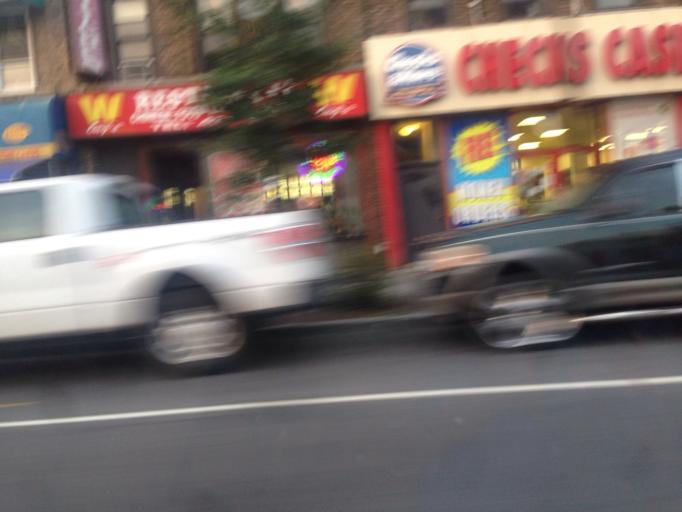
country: US
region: New York
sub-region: Kings County
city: Brooklyn
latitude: 40.6336
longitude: -73.9484
